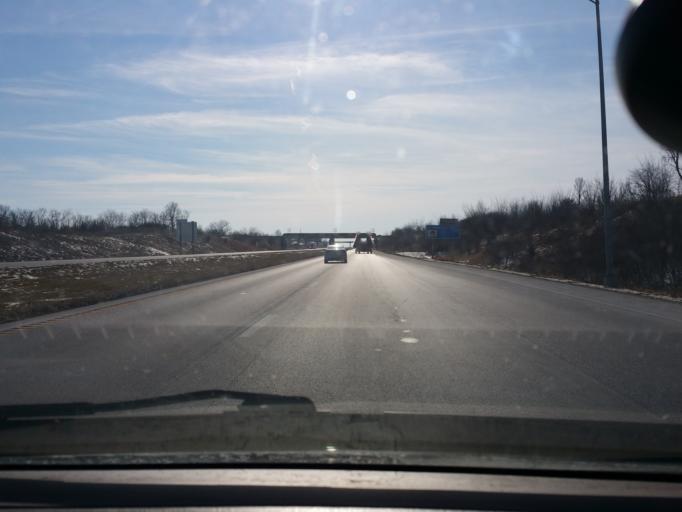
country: US
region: Missouri
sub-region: Clinton County
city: Cameron
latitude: 39.7497
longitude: -94.2202
